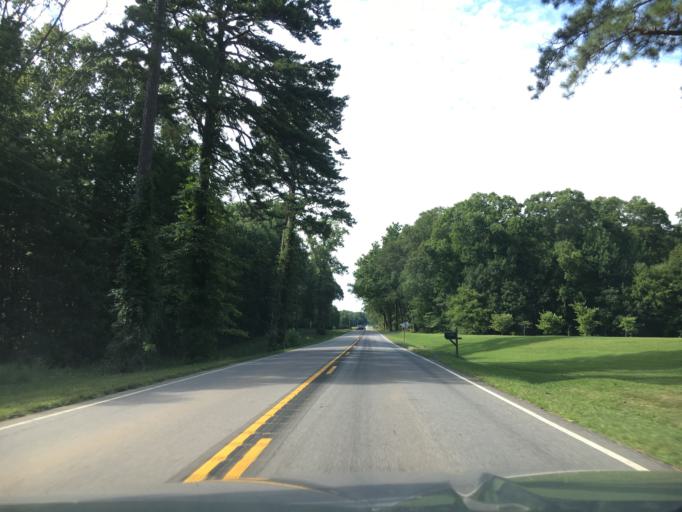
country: US
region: Virginia
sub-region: Halifax County
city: Mountain Road
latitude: 36.8839
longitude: -79.0156
